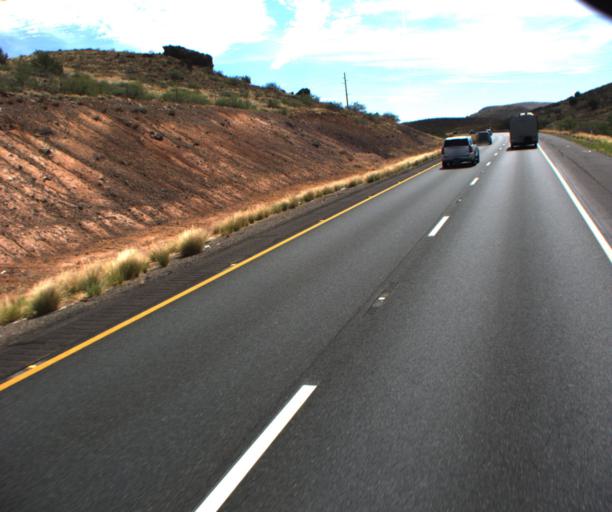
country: US
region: Arizona
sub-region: Yavapai County
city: Cordes Lakes
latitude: 34.4216
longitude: -112.0557
